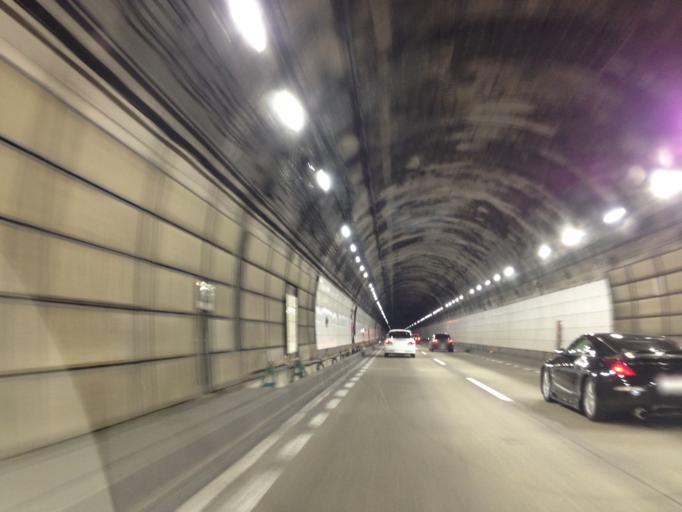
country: JP
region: Miyagi
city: Sendai
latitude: 38.2625
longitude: 140.8487
